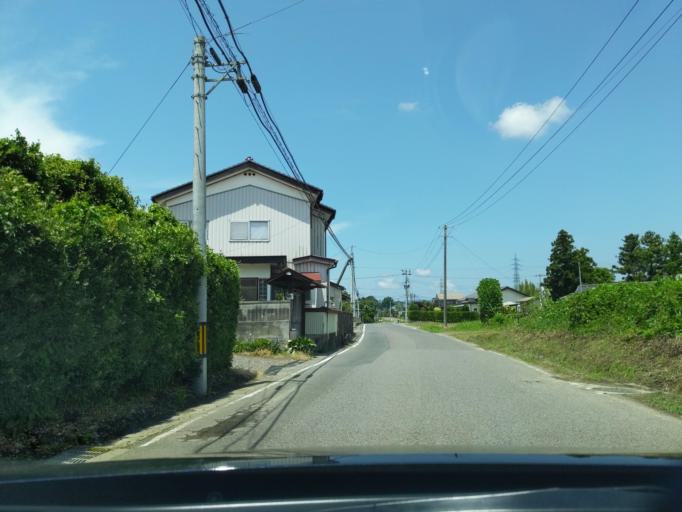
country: JP
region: Fukushima
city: Sukagawa
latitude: 37.3341
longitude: 140.3578
